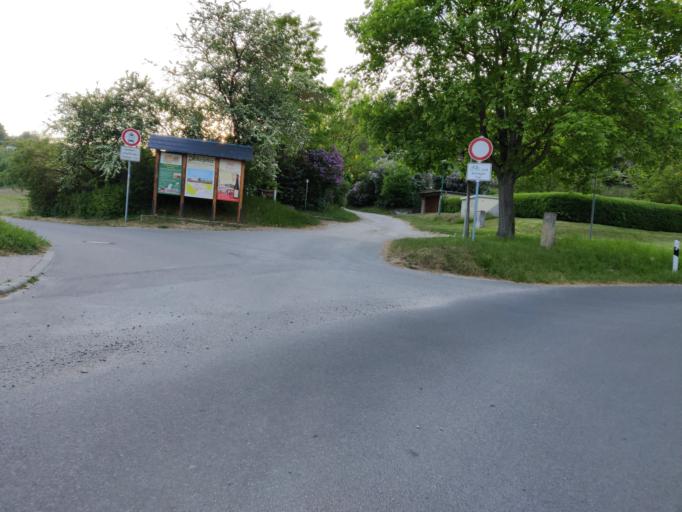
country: DE
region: Saxony-Anhalt
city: Balgstadt
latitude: 51.2140
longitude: 11.7462
